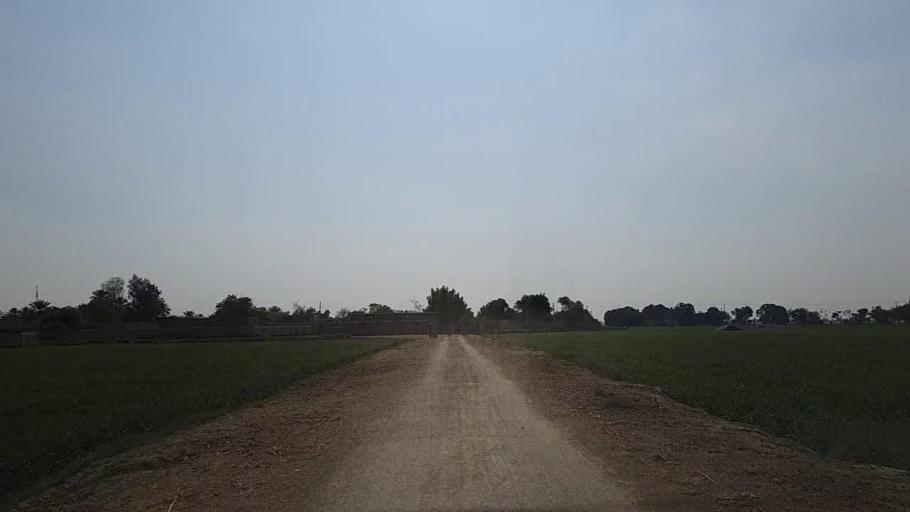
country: PK
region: Sindh
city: Nawabshah
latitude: 26.2514
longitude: 68.4919
